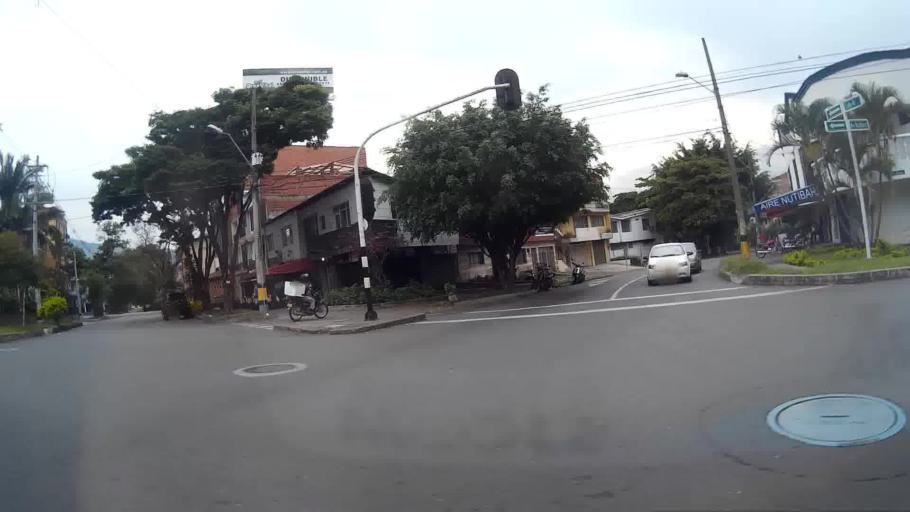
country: CO
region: Antioquia
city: Medellin
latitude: 6.2478
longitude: -75.5976
